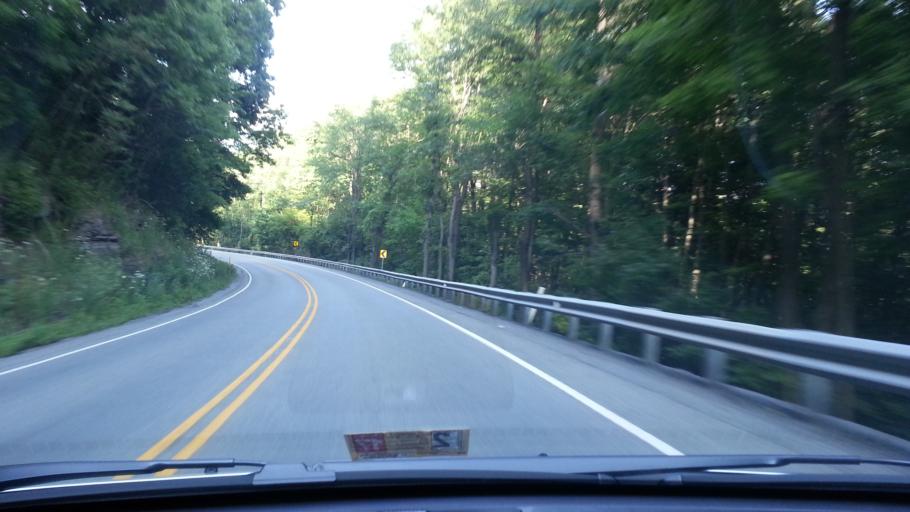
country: US
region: Pennsylvania
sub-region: Elk County
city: Saint Marys
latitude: 41.2432
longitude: -78.5308
